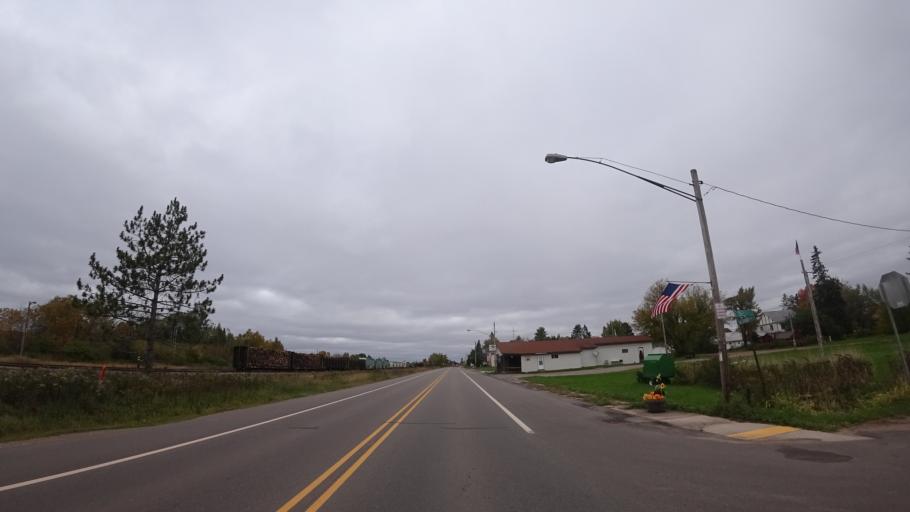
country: US
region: Michigan
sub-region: Iron County
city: Crystal Falls
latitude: 46.1406
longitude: -88.0938
